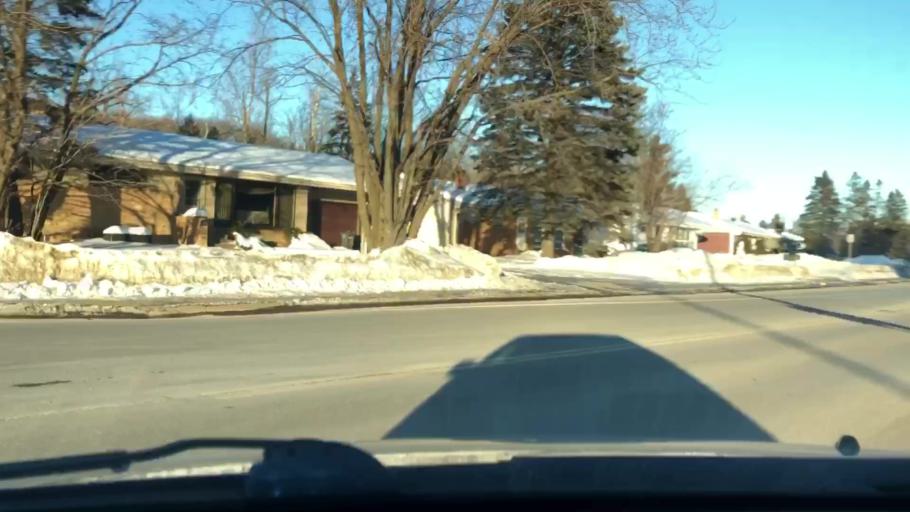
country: US
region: Minnesota
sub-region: Saint Louis County
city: Duluth
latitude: 46.8221
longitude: -92.0976
